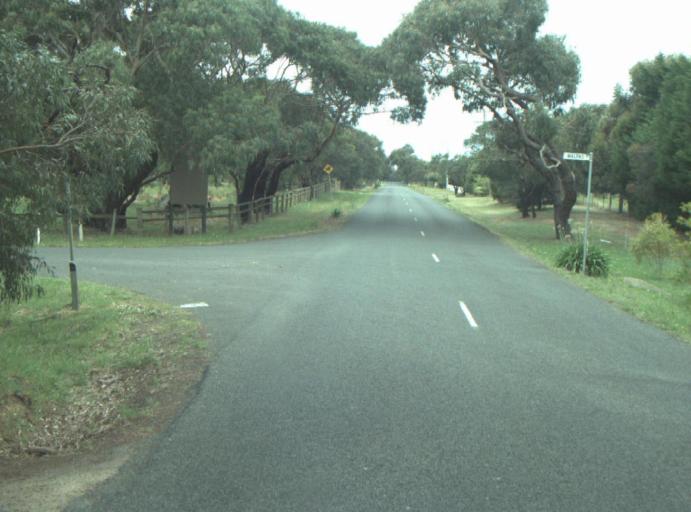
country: AU
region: Victoria
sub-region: Greater Geelong
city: Breakwater
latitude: -38.2035
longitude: 144.4158
